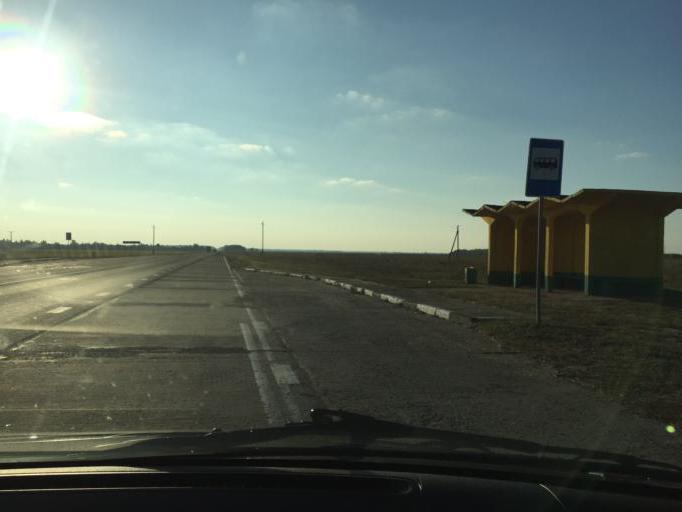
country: BY
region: Brest
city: Asnyezhytsy
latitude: 52.2731
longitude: 26.3785
